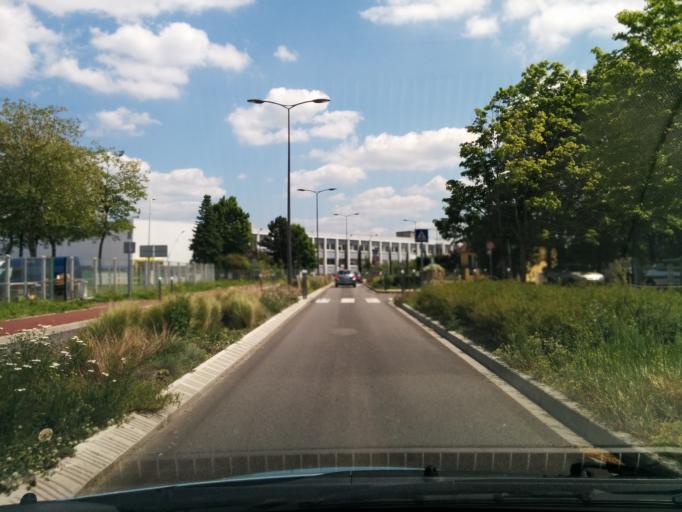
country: FR
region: Ile-de-France
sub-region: Departement des Yvelines
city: Juziers
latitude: 48.9762
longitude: 1.8516
